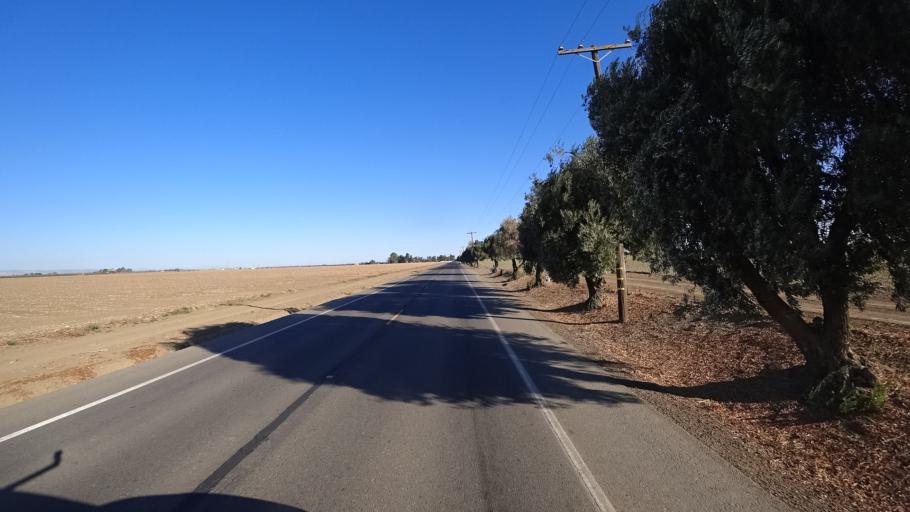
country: US
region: California
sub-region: Yolo County
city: Woodland
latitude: 38.6090
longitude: -121.7853
